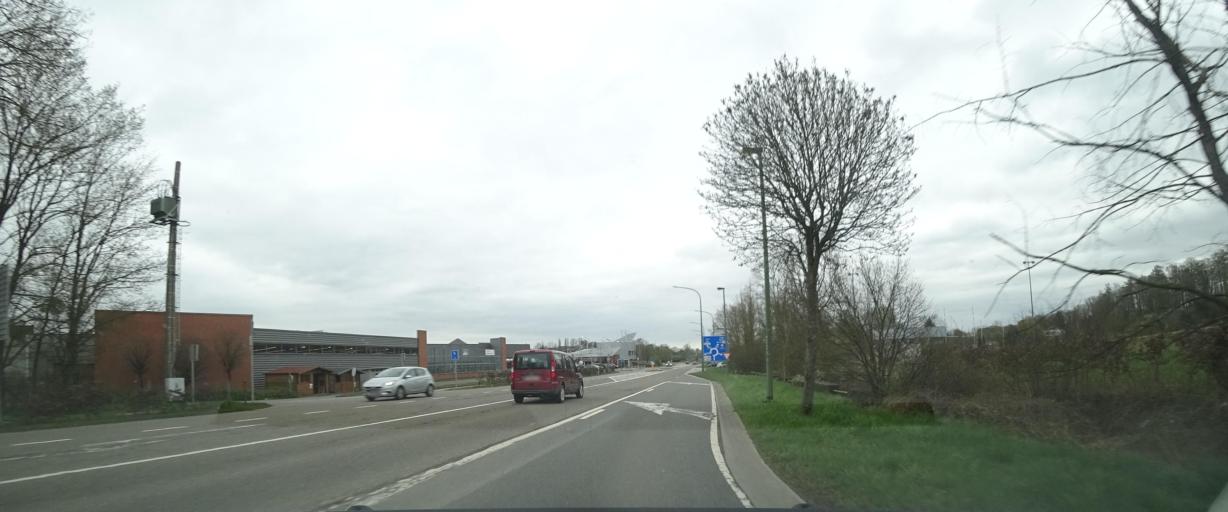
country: BE
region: Wallonia
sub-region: Province du Luxembourg
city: Marche-en-Famenne
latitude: 50.2211
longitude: 5.3335
